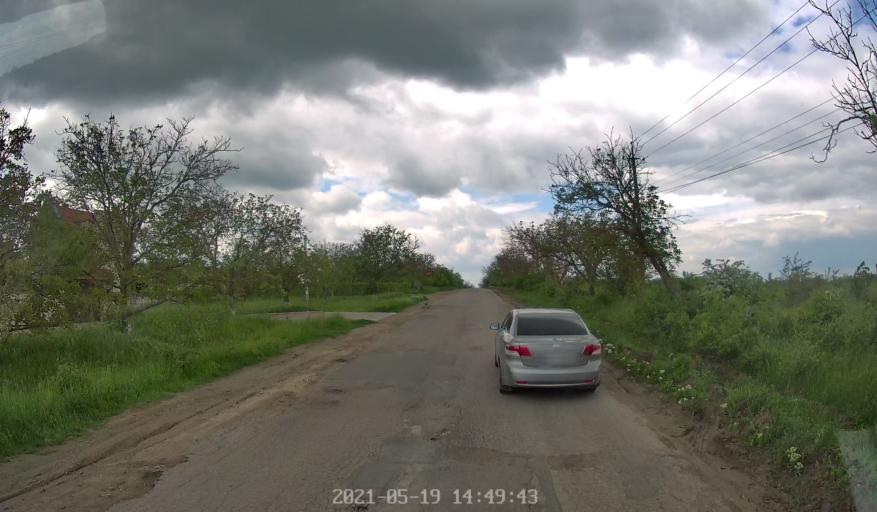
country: MD
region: Chisinau
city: Stauceni
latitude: 47.0520
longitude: 28.9495
